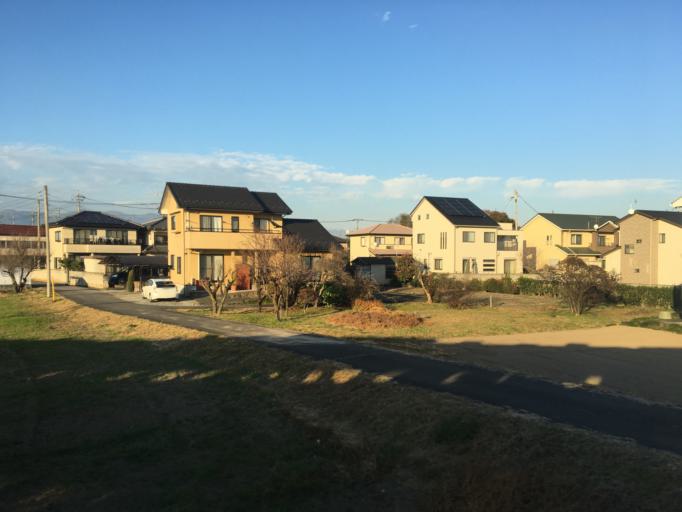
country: JP
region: Gunma
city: Isesaki
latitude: 36.3473
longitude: 139.1560
